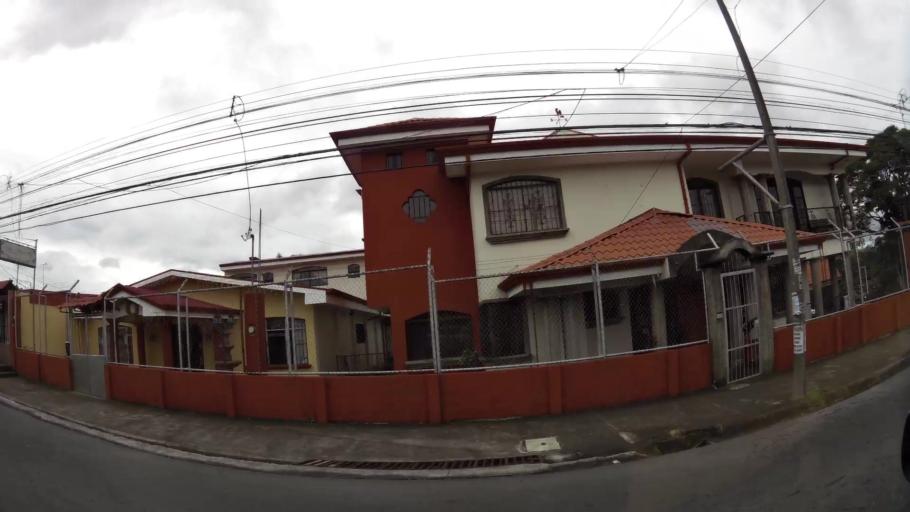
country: CR
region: San Jose
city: Calle Blancos
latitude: 9.9492
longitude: -84.0693
